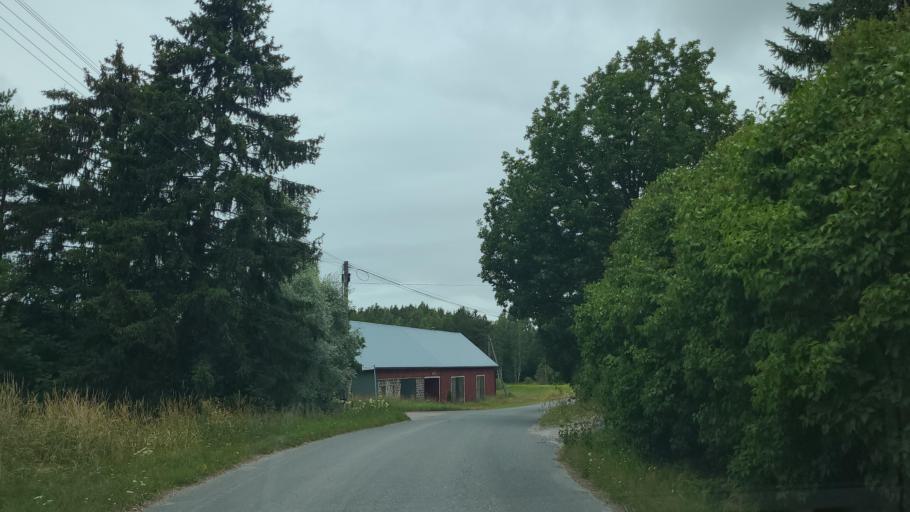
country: FI
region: Varsinais-Suomi
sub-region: Aboland-Turunmaa
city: Dragsfjaerd
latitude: 60.0735
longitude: 22.4508
